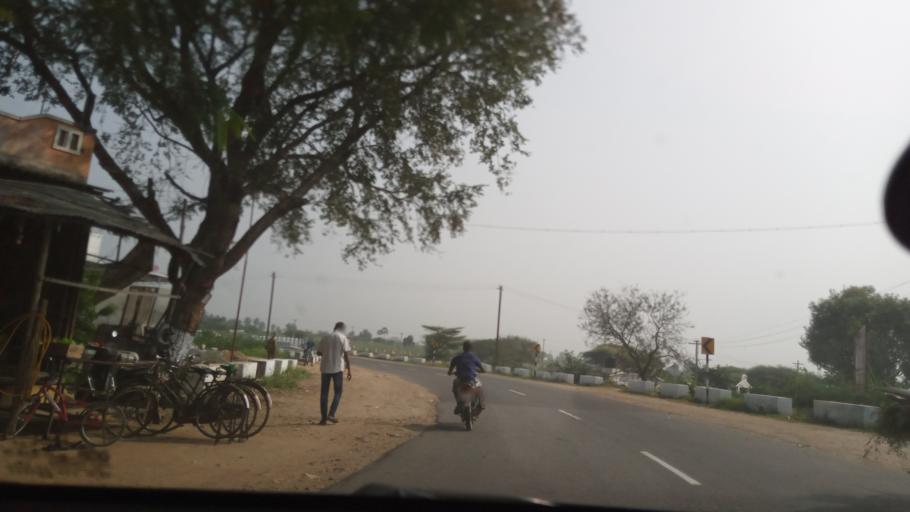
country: IN
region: Tamil Nadu
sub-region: Erode
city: Punjai Puliyampatti
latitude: 11.4041
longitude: 77.1920
